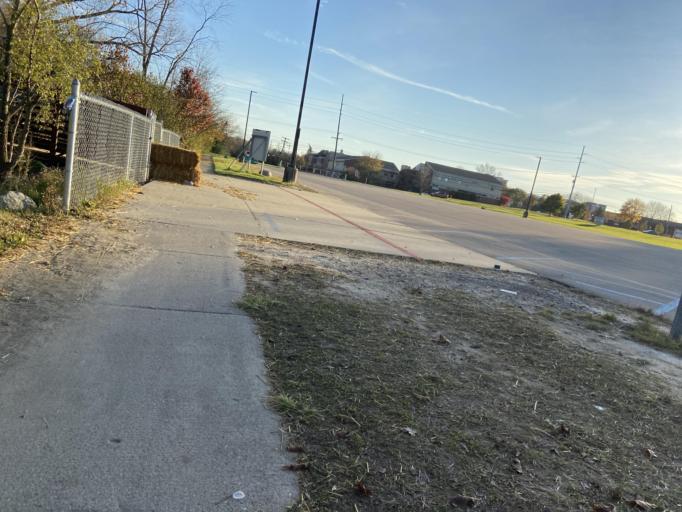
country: US
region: Michigan
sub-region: Oakland County
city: Farmington Hills
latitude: 42.4999
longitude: -83.3733
